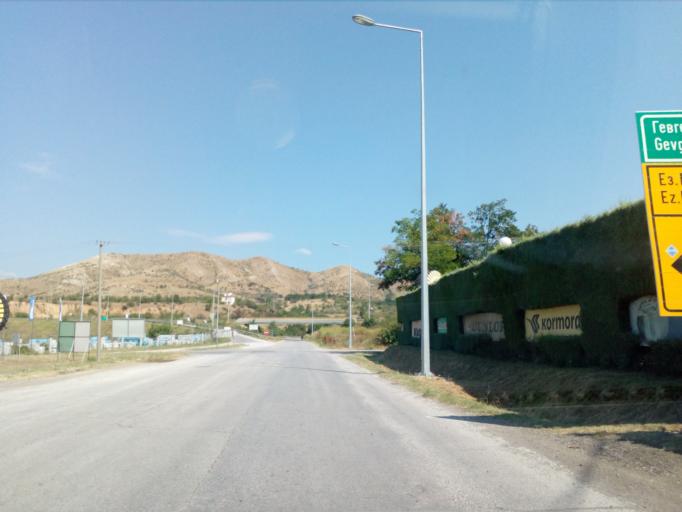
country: MK
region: Veles
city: Veles
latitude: 41.7473
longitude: 21.7702
